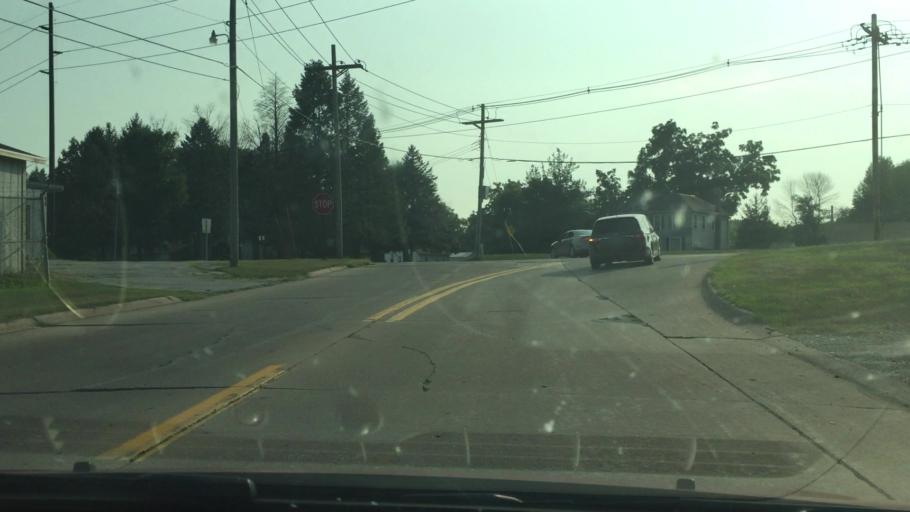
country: US
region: Iowa
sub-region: Muscatine County
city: Muscatine
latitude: 41.4439
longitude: -91.0414
